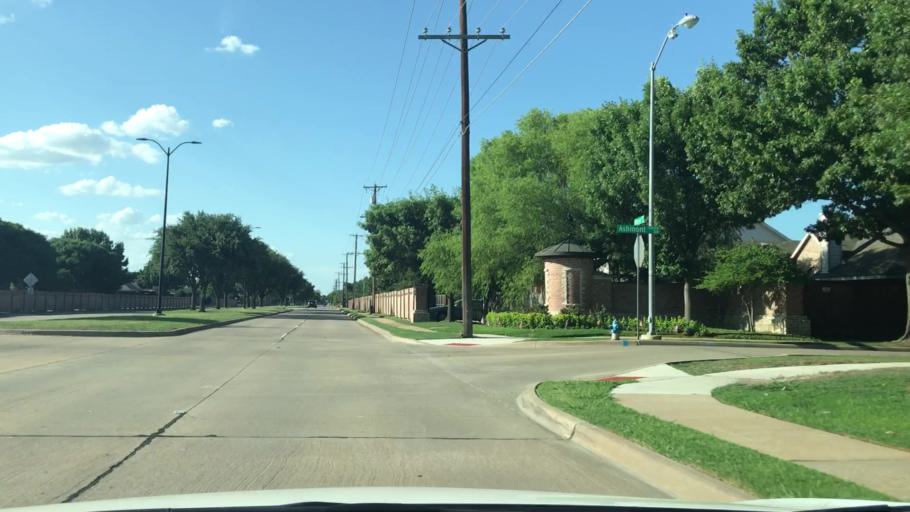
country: US
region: Texas
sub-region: Collin County
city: Frisco
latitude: 33.1102
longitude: -96.7881
